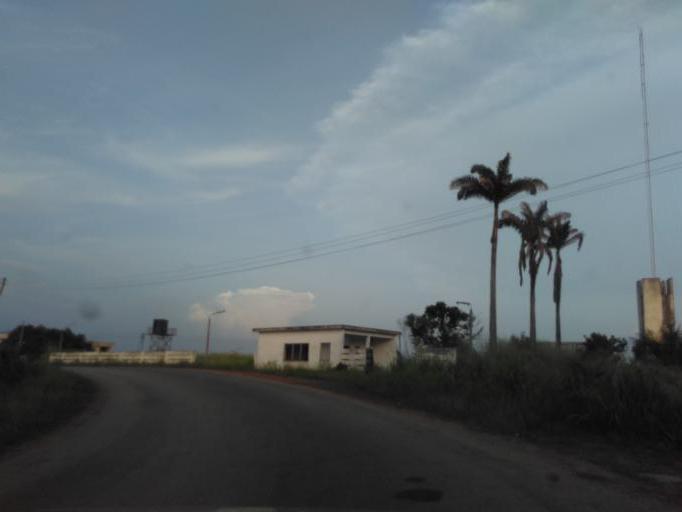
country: GH
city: Bekwai
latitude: 6.5400
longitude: -1.4418
